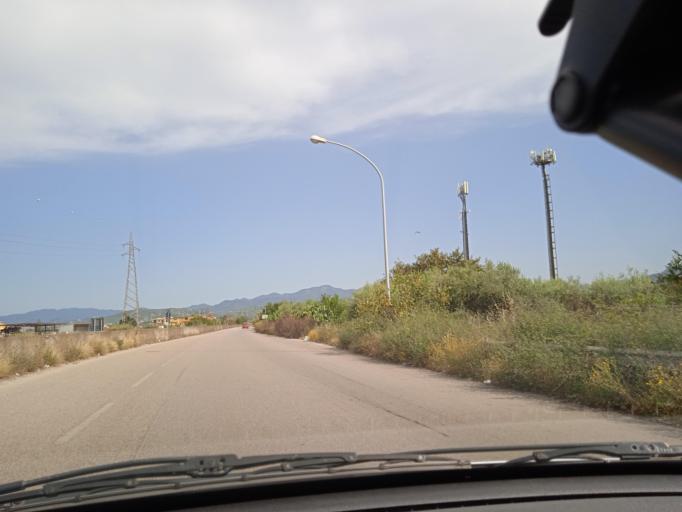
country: IT
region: Sicily
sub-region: Messina
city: Milazzo
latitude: 38.1965
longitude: 15.2543
